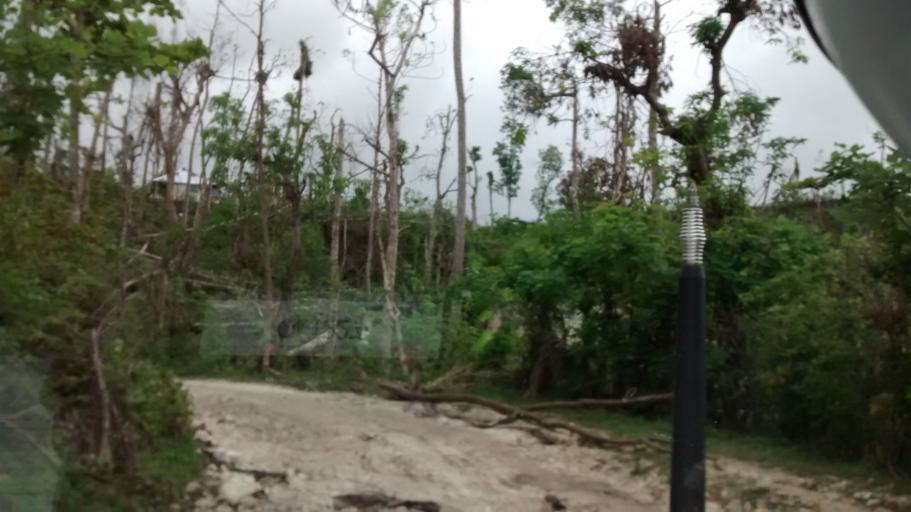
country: HT
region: Grandans
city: Jeremie
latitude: 18.5652
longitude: -74.1527
